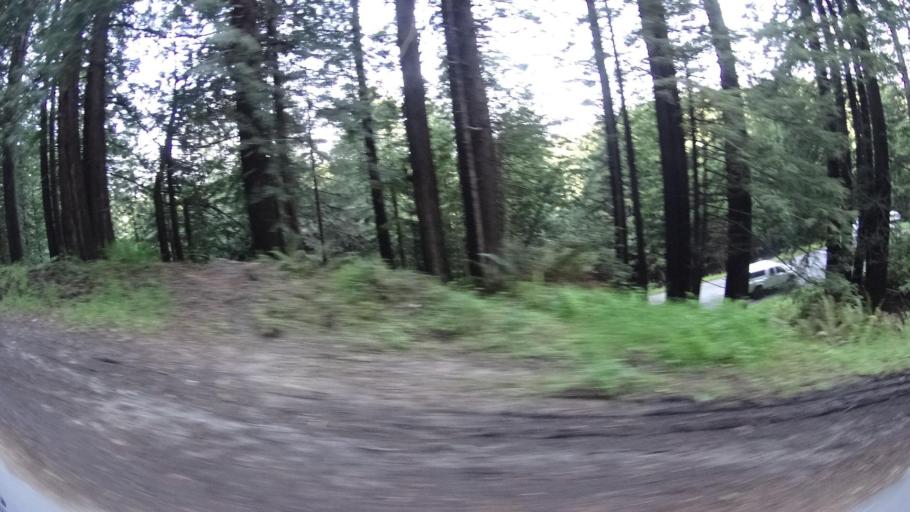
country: US
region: California
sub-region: Humboldt County
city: Bayside
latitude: 40.7569
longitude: -124.0473
